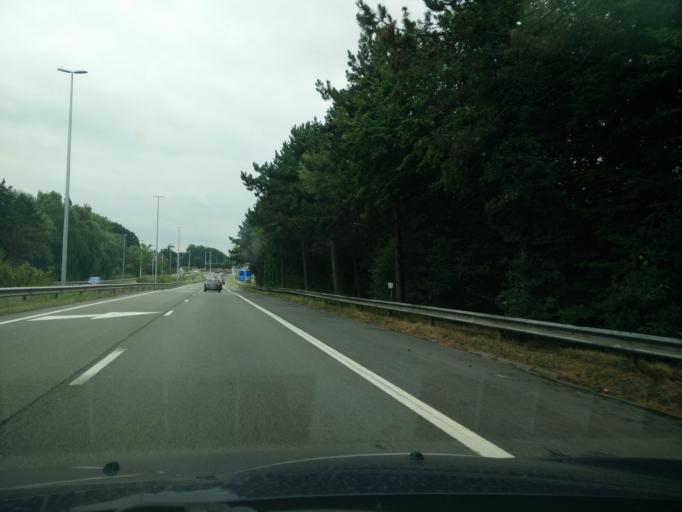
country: BE
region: Flanders
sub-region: Provincie Oost-Vlaanderen
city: Oudenaarde
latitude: 50.8357
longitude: 3.5995
